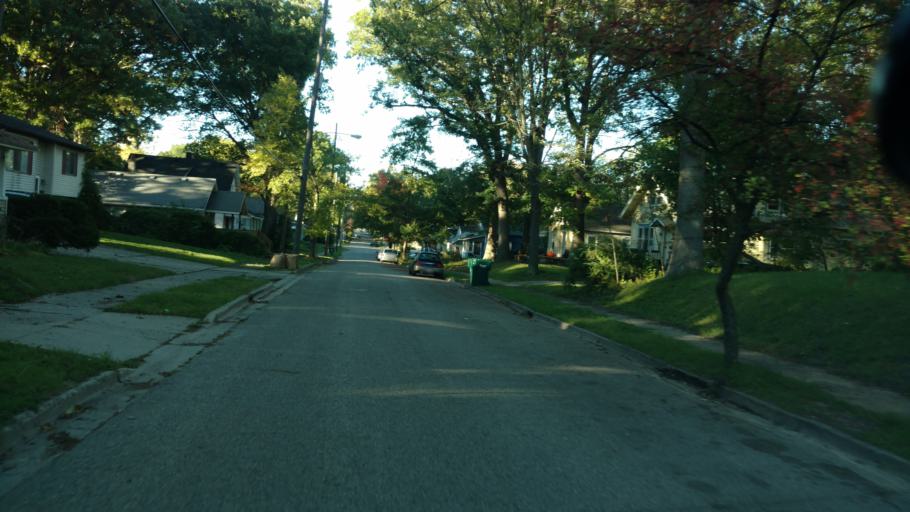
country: US
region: Michigan
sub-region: Ingham County
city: Lansing
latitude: 42.7259
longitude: -84.5250
